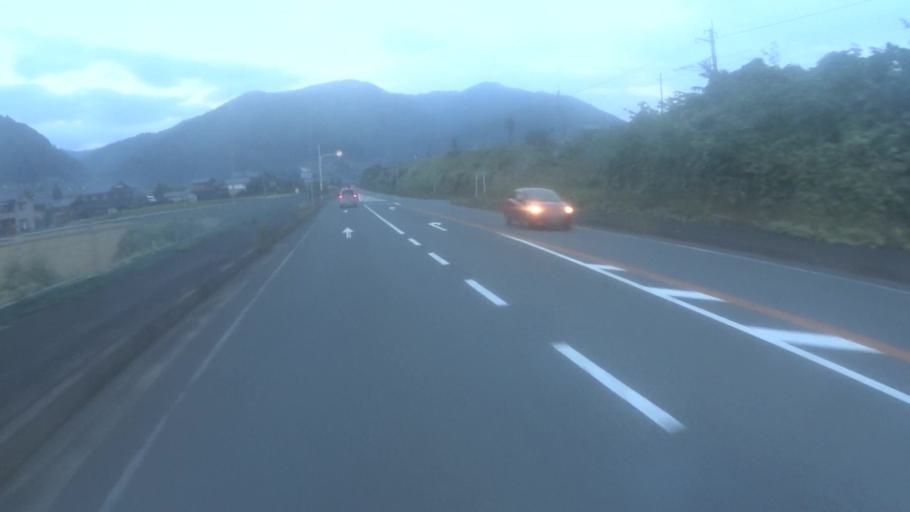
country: JP
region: Kyoto
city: Ayabe
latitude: 35.2674
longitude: 135.3881
